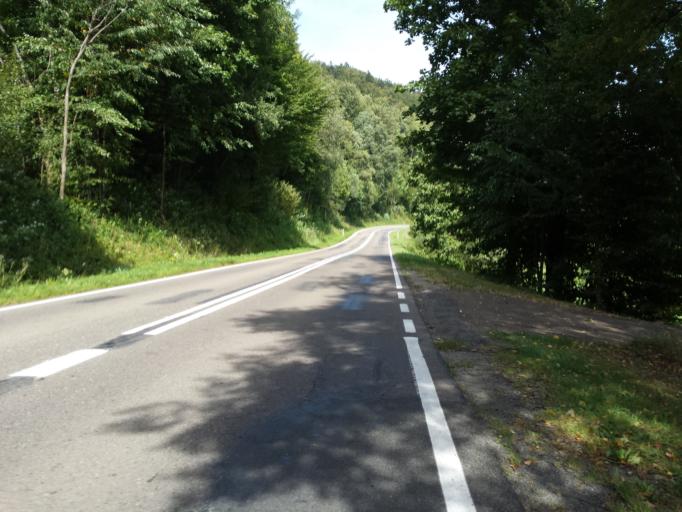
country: PL
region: Subcarpathian Voivodeship
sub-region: Powiat leski
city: Baligrod
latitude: 49.3662
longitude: 22.2731
